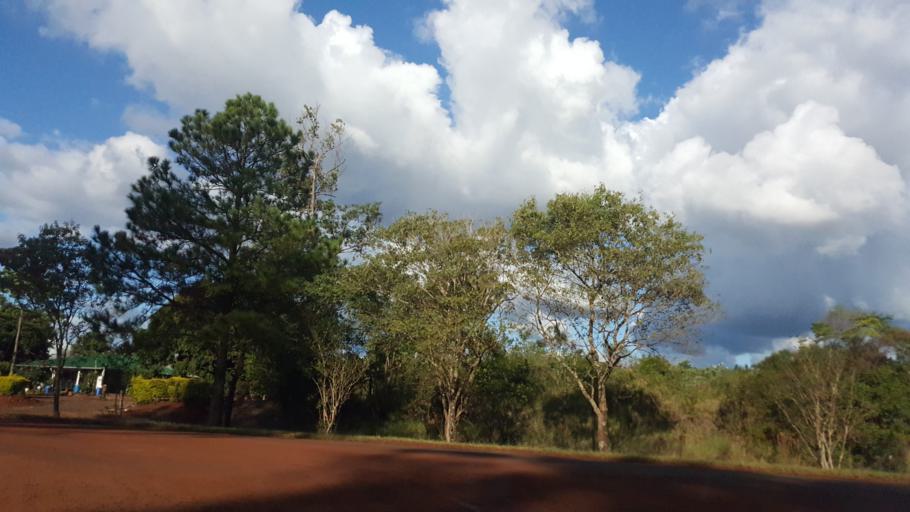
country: AR
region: Misiones
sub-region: Departamento de Capital
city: Posadas
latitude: -27.4224
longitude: -55.9955
